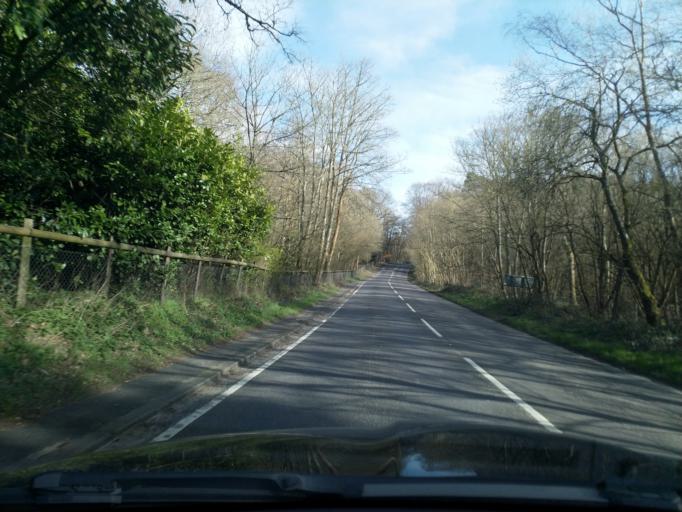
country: GB
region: England
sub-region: Hampshire
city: Aldershot
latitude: 51.2657
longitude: -0.7832
